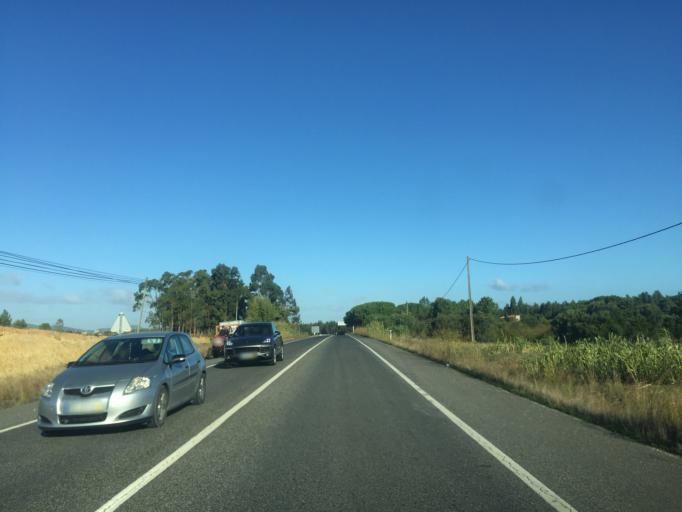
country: PT
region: Lisbon
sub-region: Azambuja
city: Aveiras de Cima
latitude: 39.1668
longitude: -8.9210
